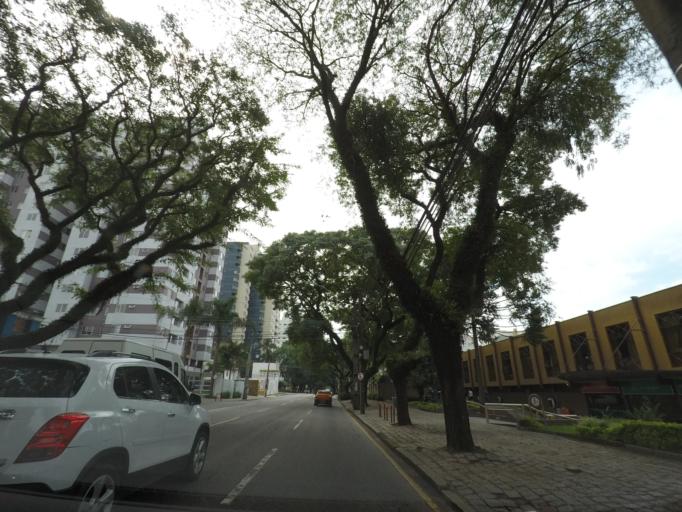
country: BR
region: Parana
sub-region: Curitiba
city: Curitiba
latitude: -25.4620
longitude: -49.2885
